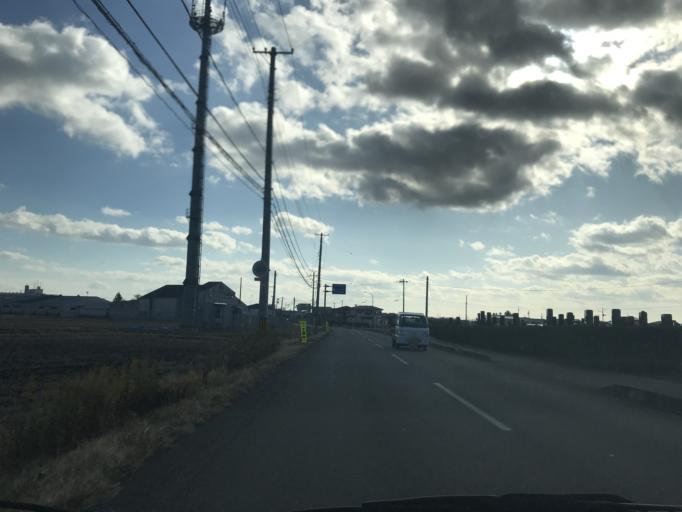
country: JP
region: Iwate
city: Ichinoseki
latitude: 38.7567
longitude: 141.0634
